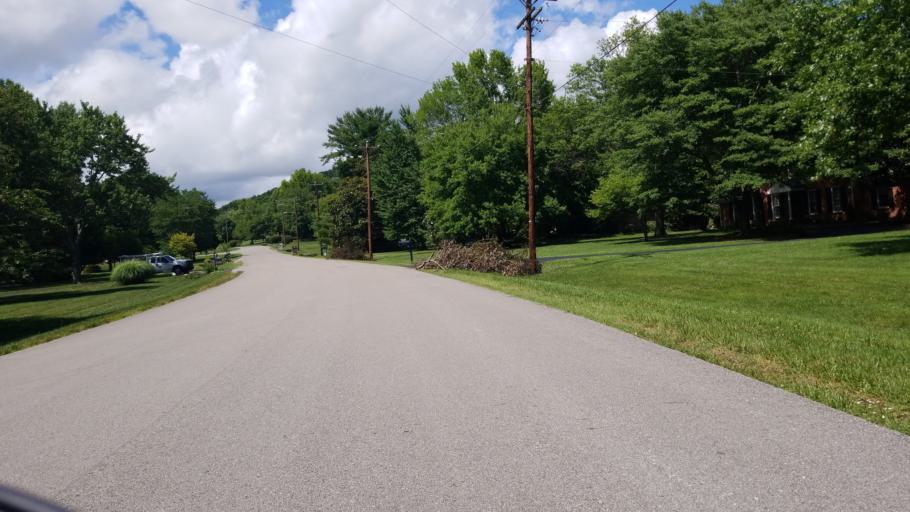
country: US
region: Tennessee
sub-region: Davidson County
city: Forest Hills
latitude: 36.0388
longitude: -86.8418
